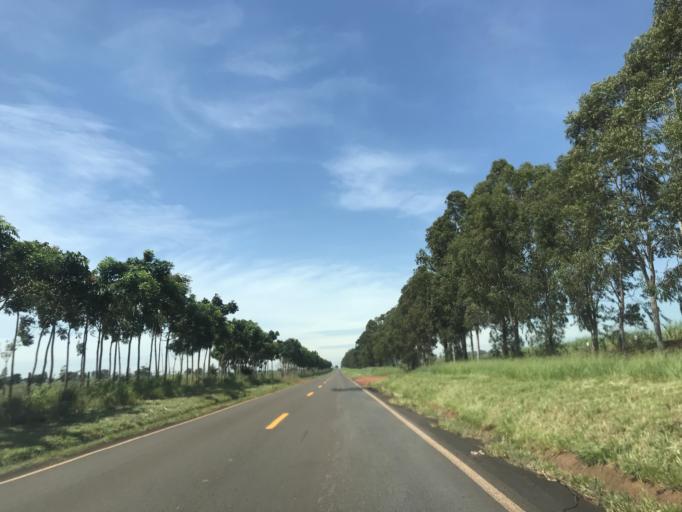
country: BR
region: Parana
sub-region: Paranavai
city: Nova Aurora
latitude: -22.8511
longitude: -52.6578
